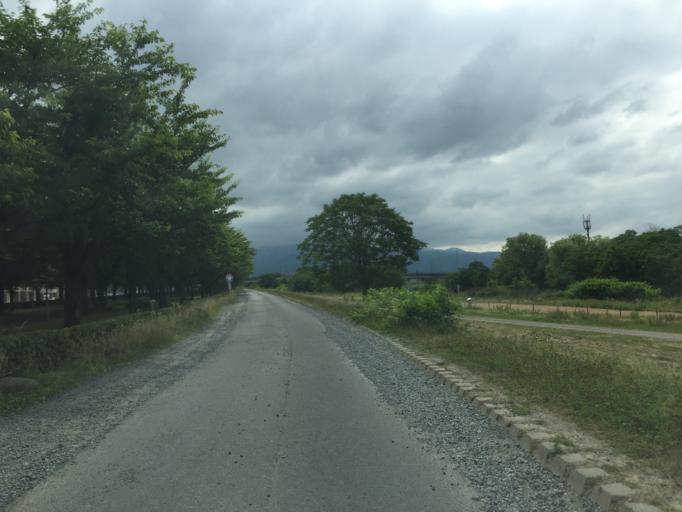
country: JP
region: Fukushima
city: Fukushima-shi
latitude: 37.7543
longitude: 140.4404
